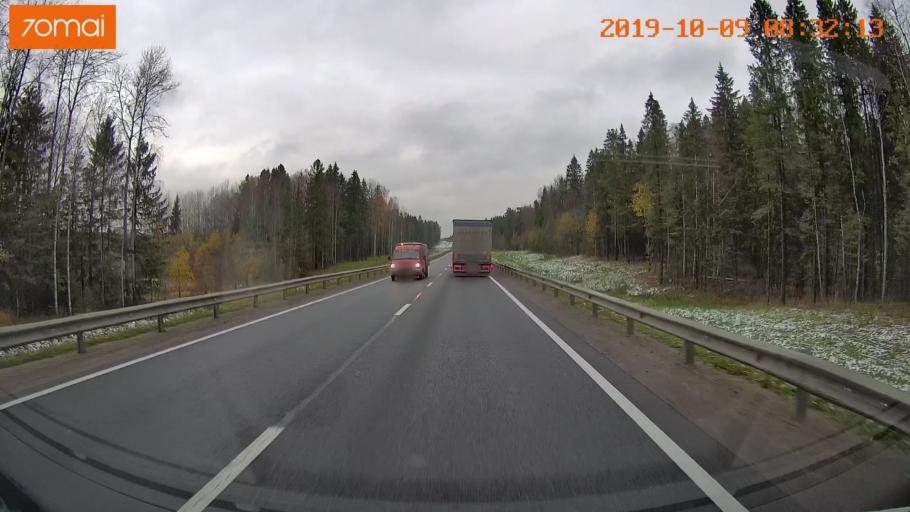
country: RU
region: Vologda
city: Gryazovets
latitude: 58.8637
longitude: 40.1983
